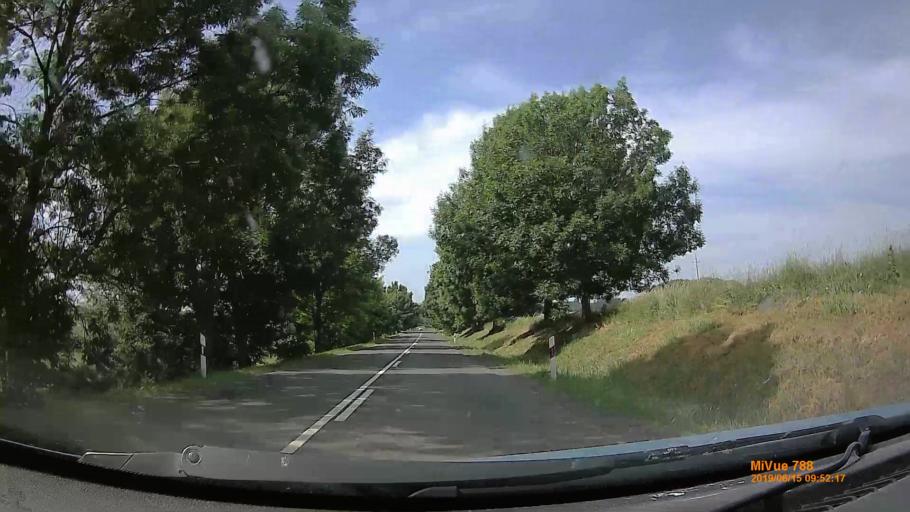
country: HU
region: Baranya
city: Sasd
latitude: 46.2770
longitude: 18.1069
